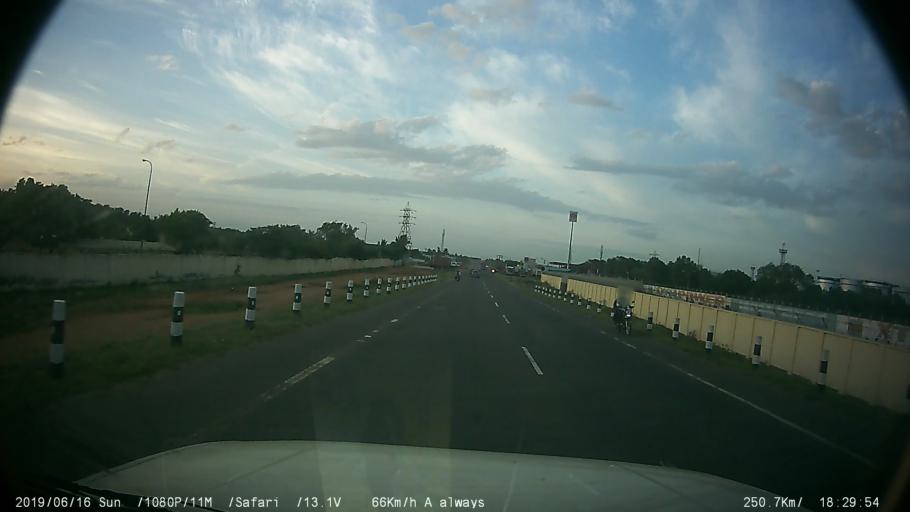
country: IN
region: Tamil Nadu
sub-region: Coimbatore
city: Irugur
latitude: 11.0259
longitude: 77.0756
